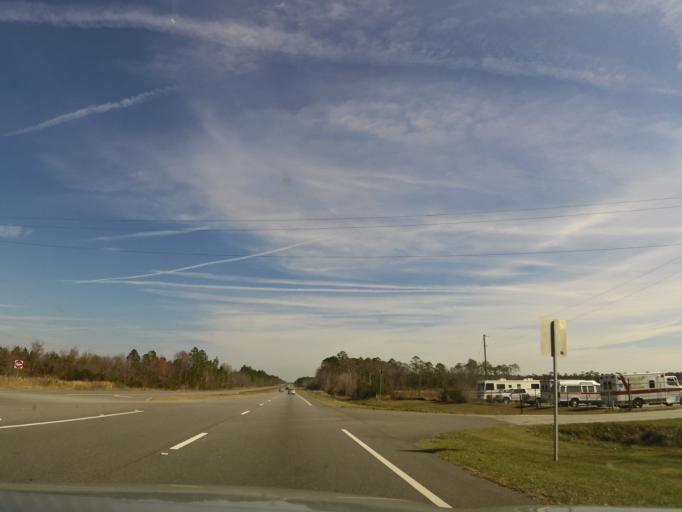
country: US
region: Georgia
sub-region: Brantley County
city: Nahunta
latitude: 31.2078
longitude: -81.9550
